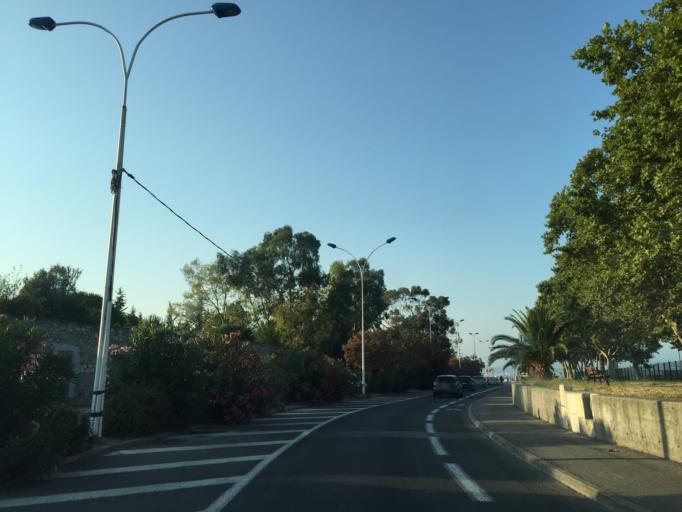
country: FR
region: Provence-Alpes-Cote d'Azur
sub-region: Departement des Alpes-Maritimes
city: Antibes
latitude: 43.5909
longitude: 7.1244
